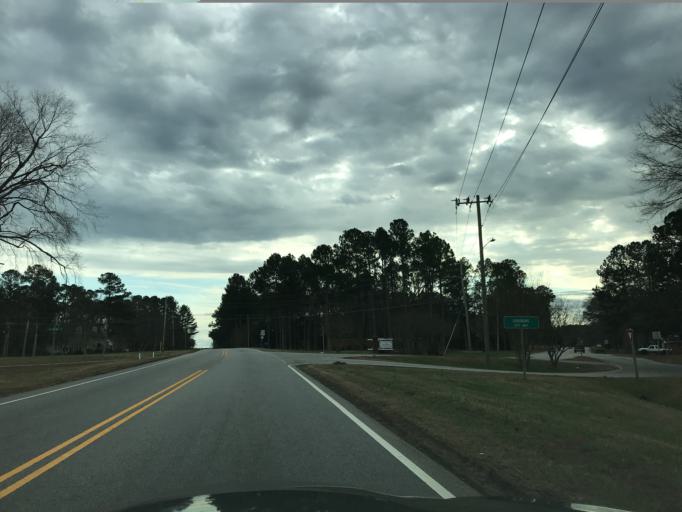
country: US
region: North Carolina
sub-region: Franklin County
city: Louisburg
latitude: 36.1172
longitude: -78.2940
